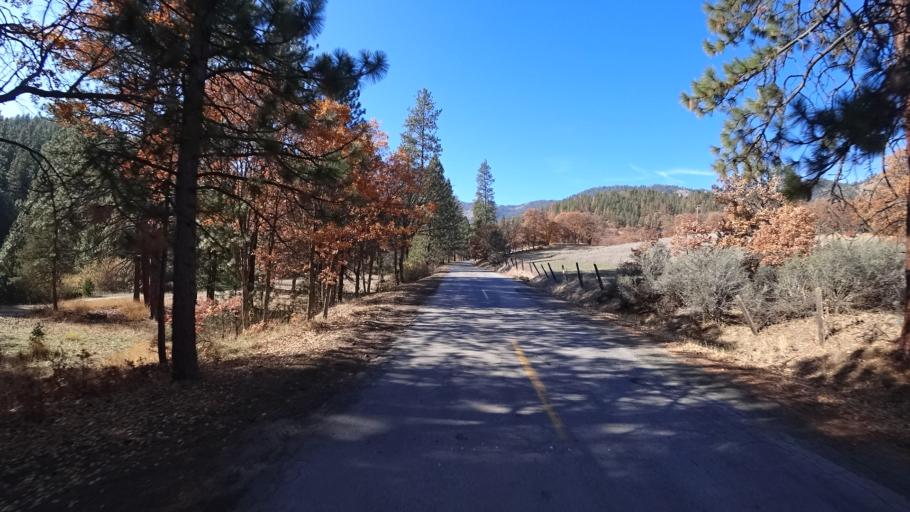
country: US
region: California
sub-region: Siskiyou County
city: Yreka
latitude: 41.7213
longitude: -122.6906
